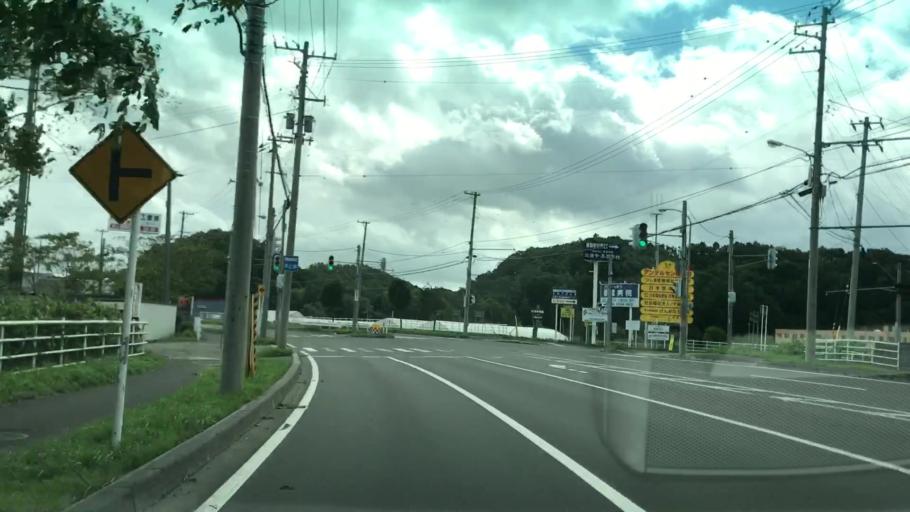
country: JP
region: Hokkaido
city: Sapporo
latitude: 42.9795
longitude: 141.4390
